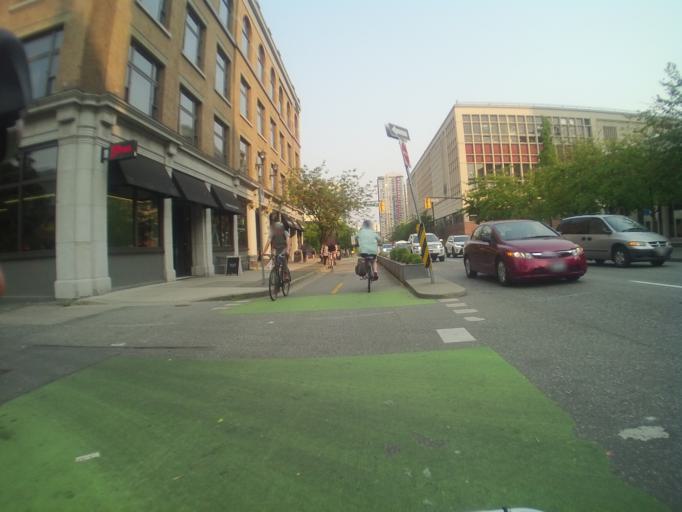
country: CA
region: British Columbia
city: West End
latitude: 49.2821
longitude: -123.1140
